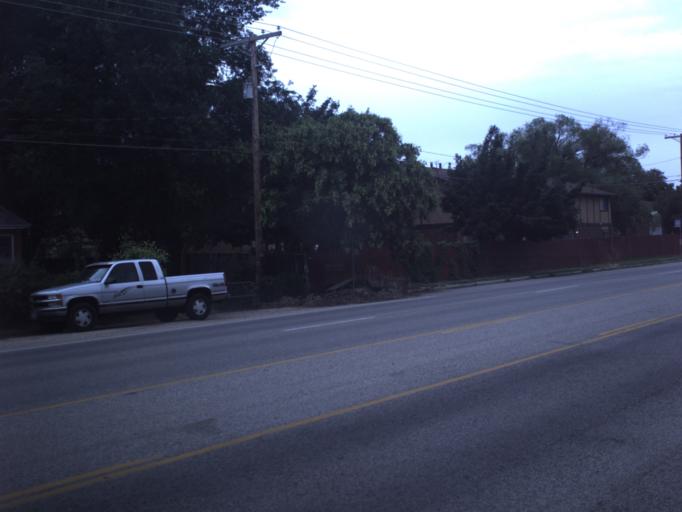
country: US
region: Utah
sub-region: Weber County
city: Harrisville
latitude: 41.2651
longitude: -111.9779
